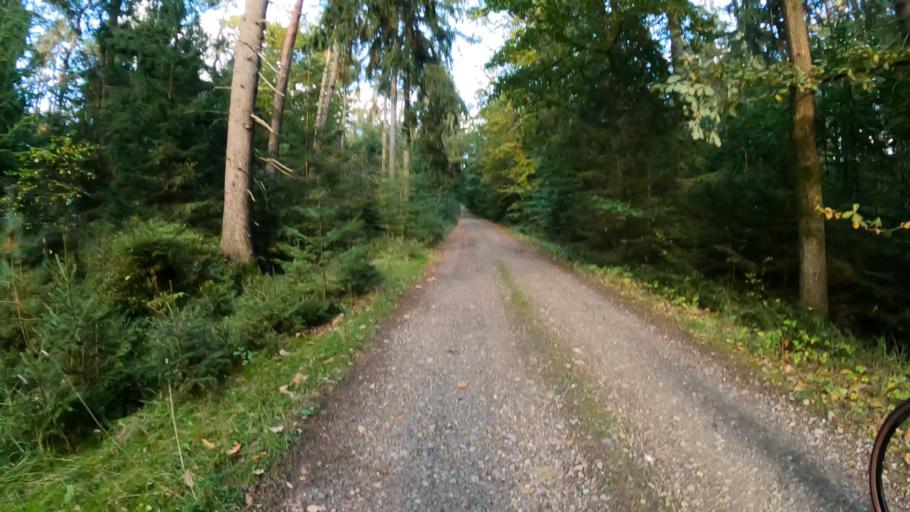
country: DE
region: Schleswig-Holstein
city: Hartenholm
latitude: 53.9151
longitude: 10.0793
